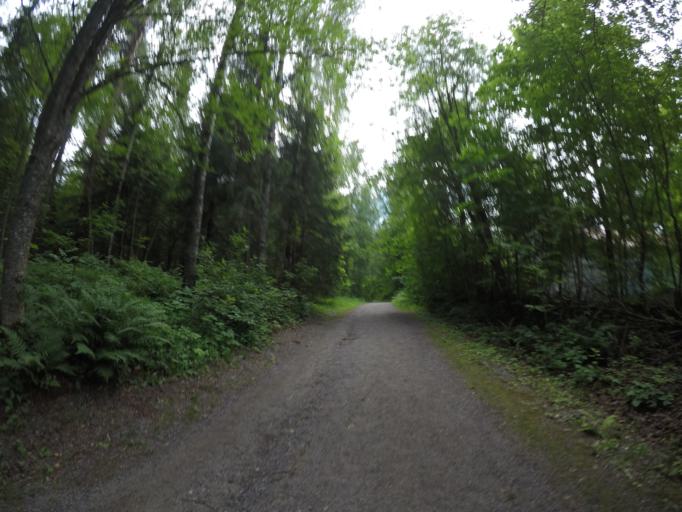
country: FI
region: Haeme
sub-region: Haemeenlinna
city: Haemeenlinna
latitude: 61.0128
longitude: 24.4479
